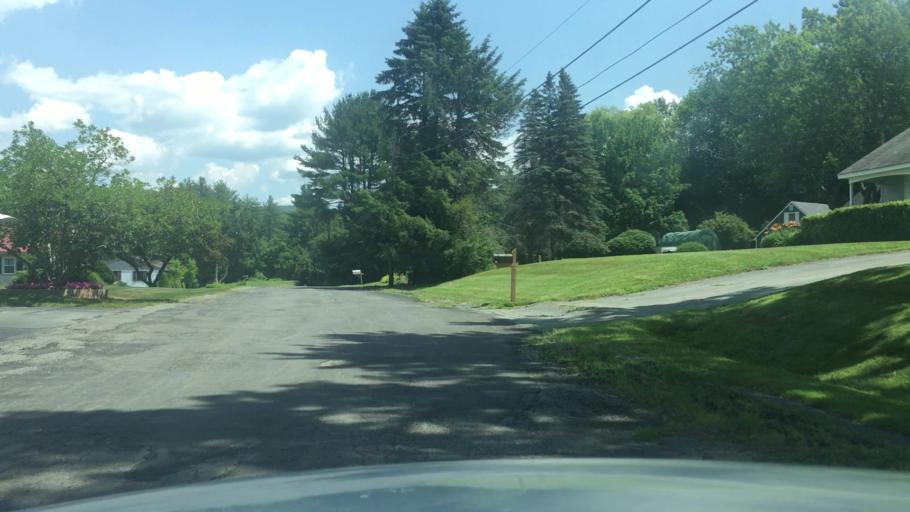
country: US
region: New Hampshire
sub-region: Grafton County
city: Lebanon
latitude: 43.6339
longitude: -72.2260
